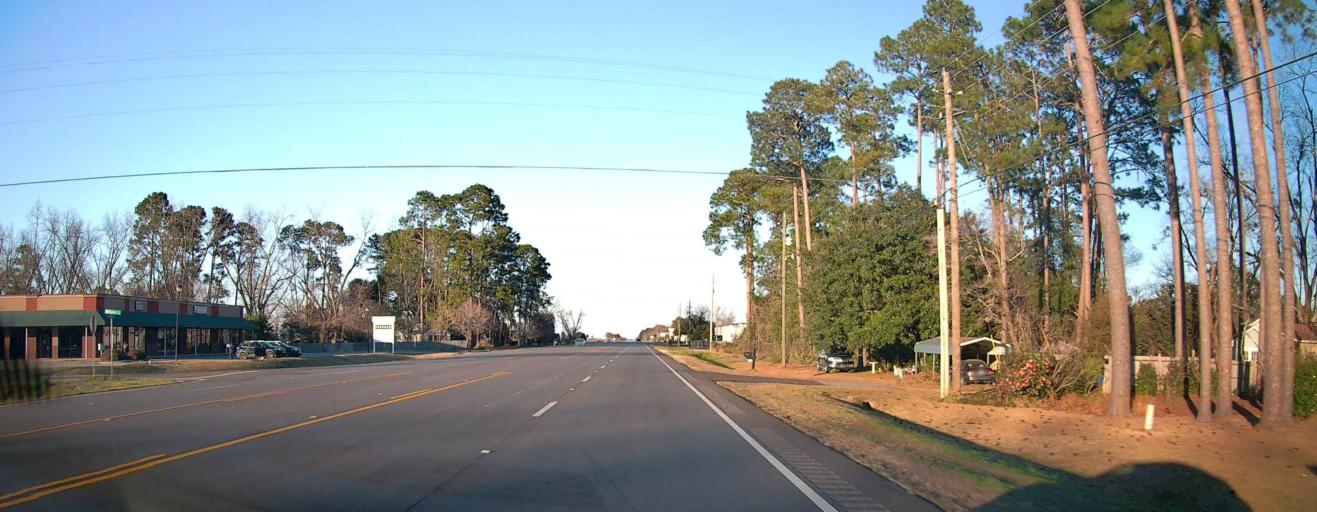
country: US
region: Georgia
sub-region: Dougherty County
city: Albany
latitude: 31.5193
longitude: -84.1968
